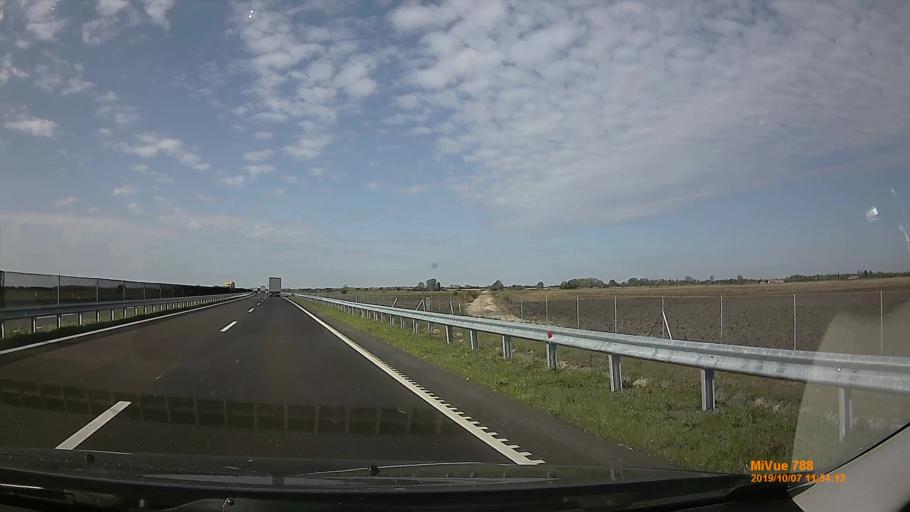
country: HU
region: Bekes
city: Szarvas
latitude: 46.8198
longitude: 20.5956
